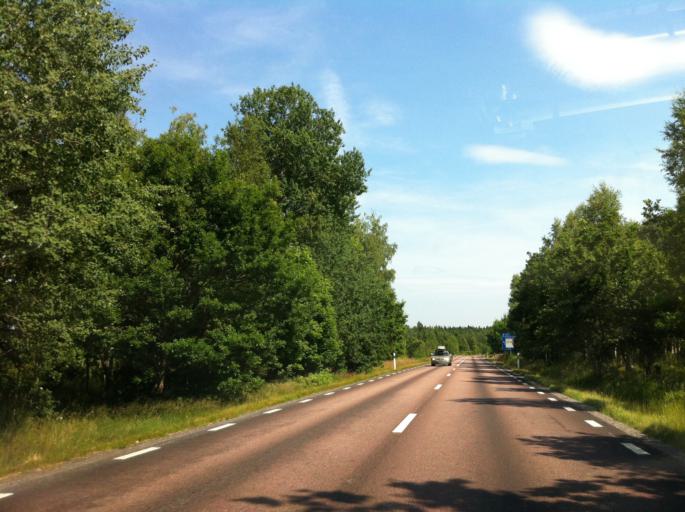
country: SE
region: Kalmar
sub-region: Nybro Kommun
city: Nybro
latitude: 56.8208
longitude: 15.7696
